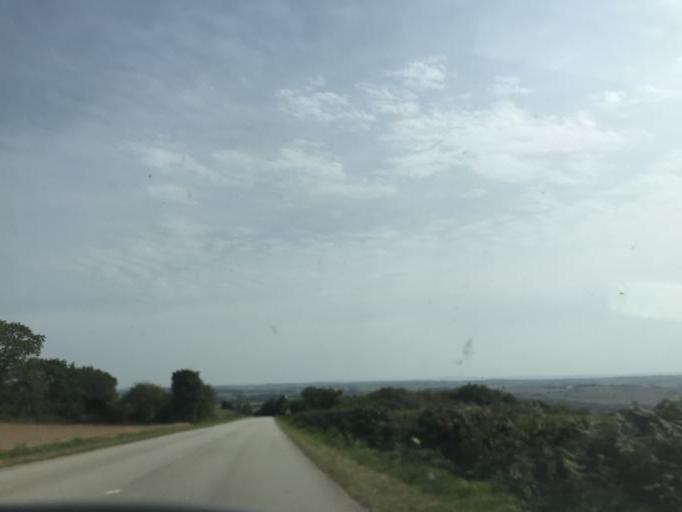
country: FR
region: Brittany
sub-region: Departement du Finistere
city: Loperec
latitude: 48.2936
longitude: -4.0551
